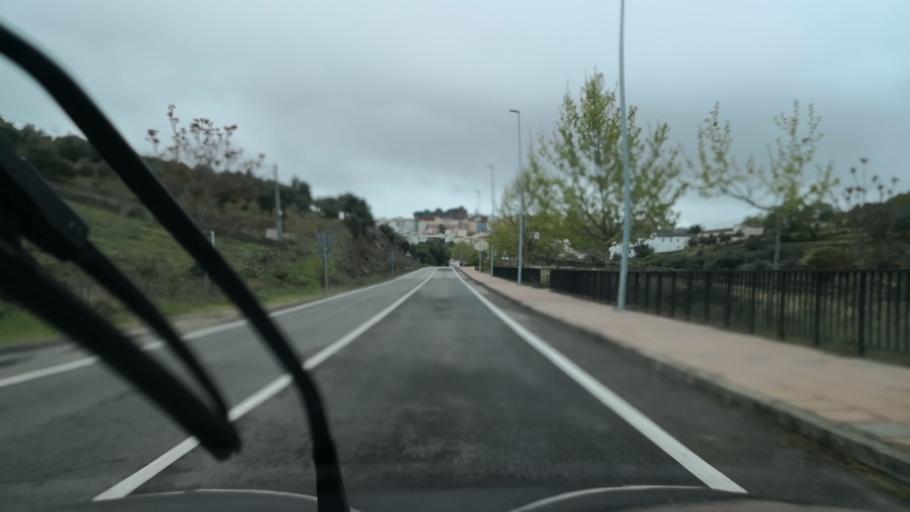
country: ES
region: Extremadura
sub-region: Provincia de Caceres
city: Caceres
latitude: 39.4847
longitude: -6.3817
